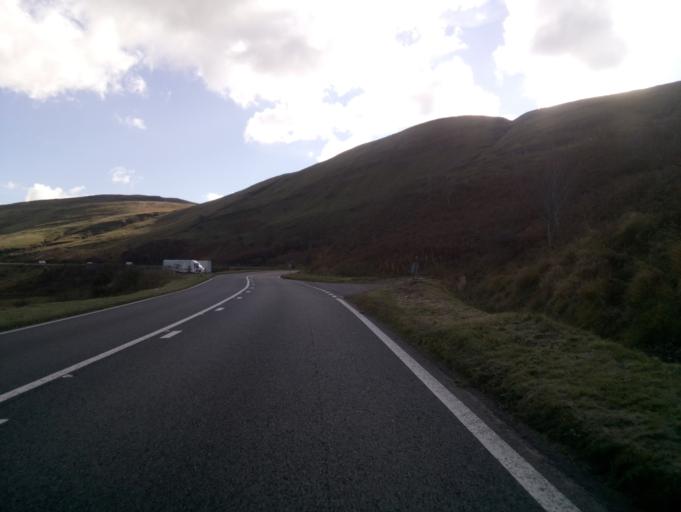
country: GB
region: Wales
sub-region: Sir Powys
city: Cray
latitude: 51.8785
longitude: -3.4951
